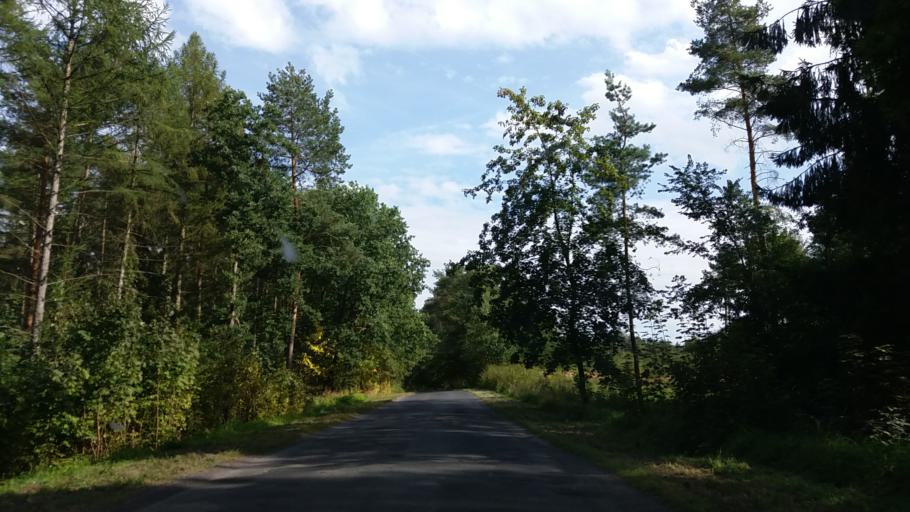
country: PL
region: West Pomeranian Voivodeship
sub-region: Powiat stargardzki
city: Dolice
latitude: 53.2286
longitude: 15.2655
